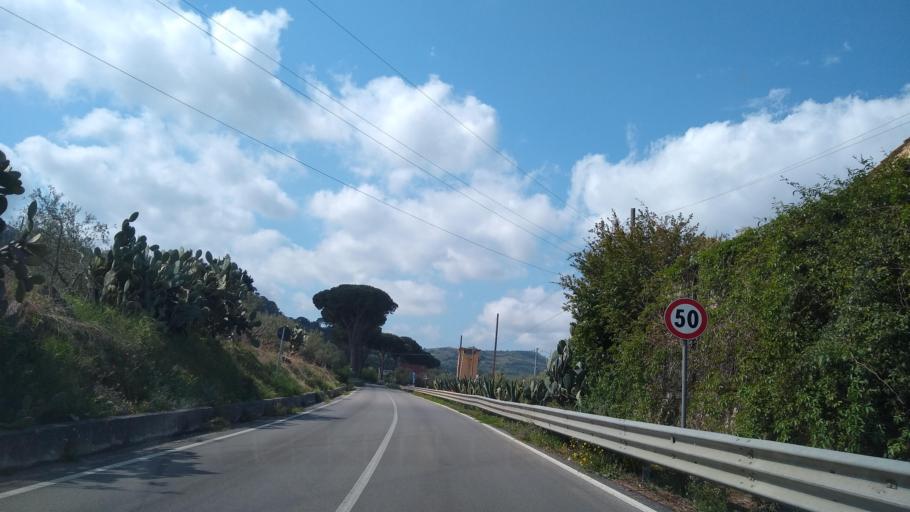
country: IT
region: Sicily
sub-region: Trapani
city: Calatafimi
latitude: 37.9397
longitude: 12.8555
